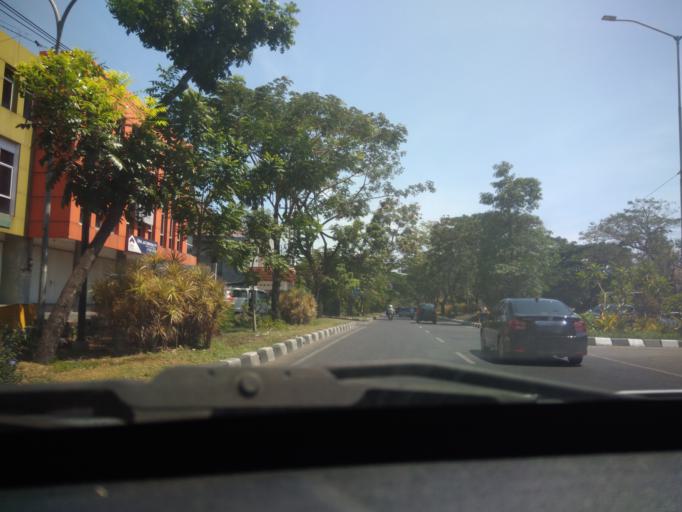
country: ID
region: East Java
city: Semampir
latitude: -7.3037
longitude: 112.7813
